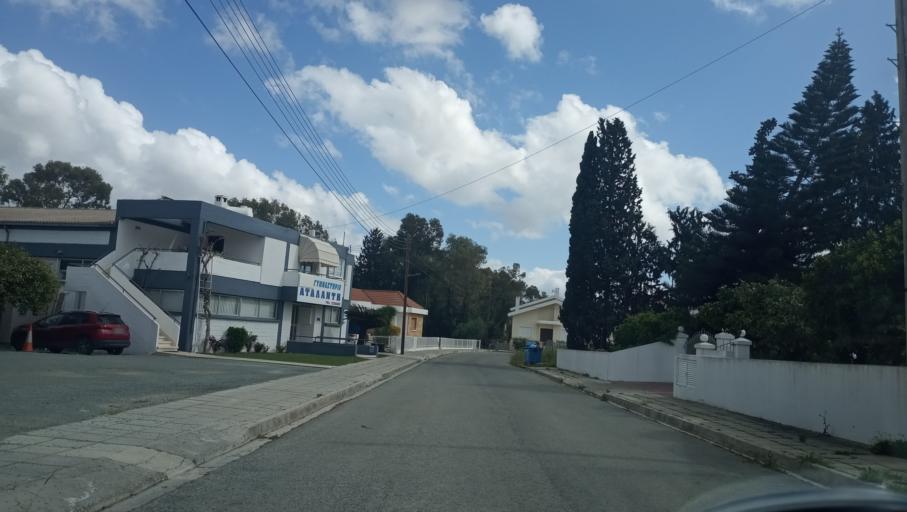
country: CY
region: Lefkosia
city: Tseri
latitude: 35.1189
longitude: 33.3097
